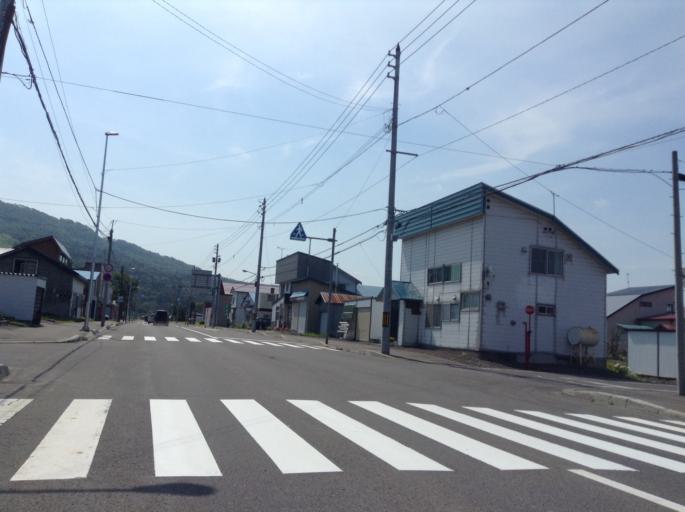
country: JP
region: Hokkaido
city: Nayoro
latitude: 44.7274
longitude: 142.2596
